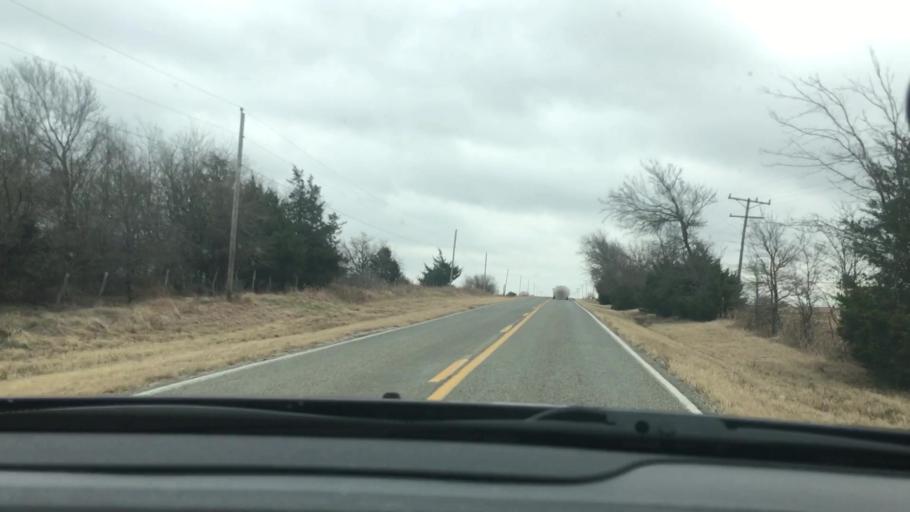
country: US
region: Oklahoma
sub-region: Johnston County
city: Tishomingo
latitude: 34.1433
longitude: -96.5397
